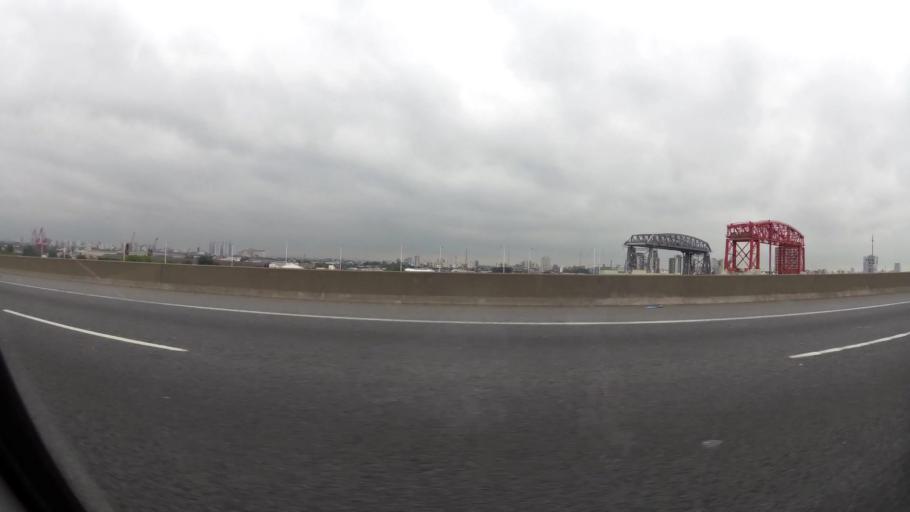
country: AR
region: Buenos Aires
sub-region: Partido de Avellaneda
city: Avellaneda
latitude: -34.6390
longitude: -58.3528
